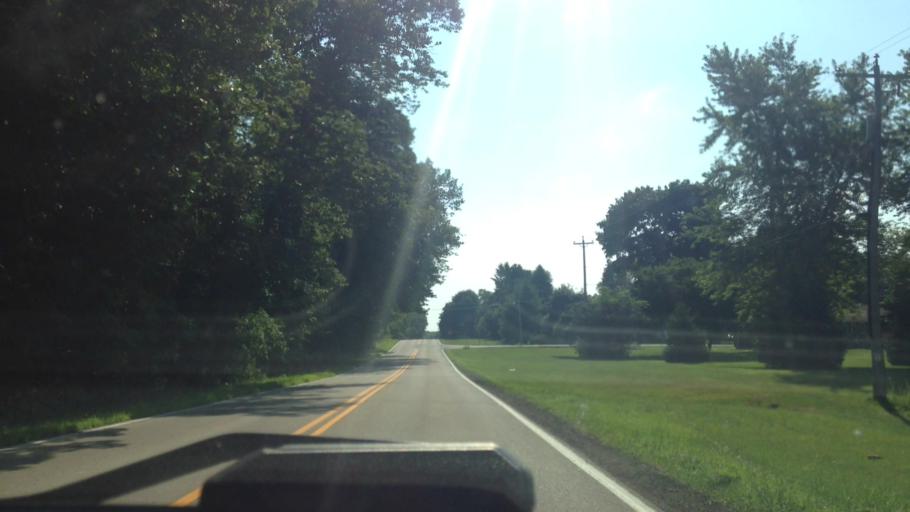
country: US
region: Wisconsin
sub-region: Waukesha County
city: Lannon
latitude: 43.1627
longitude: -88.1896
